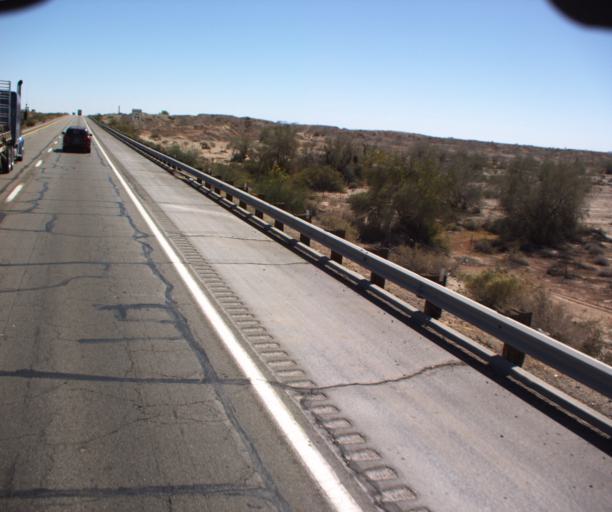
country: US
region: Arizona
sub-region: Yuma County
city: Wellton
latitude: 32.6628
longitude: -114.2669
